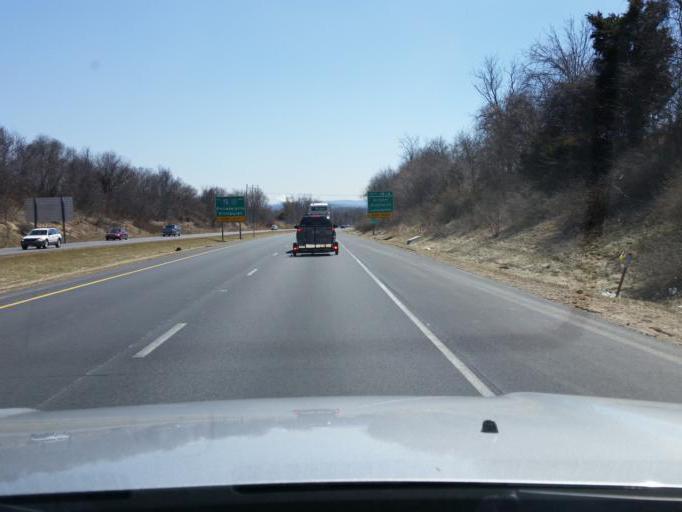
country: US
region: Pennsylvania
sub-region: Dauphin County
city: Bressler
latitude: 40.2360
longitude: -76.7993
